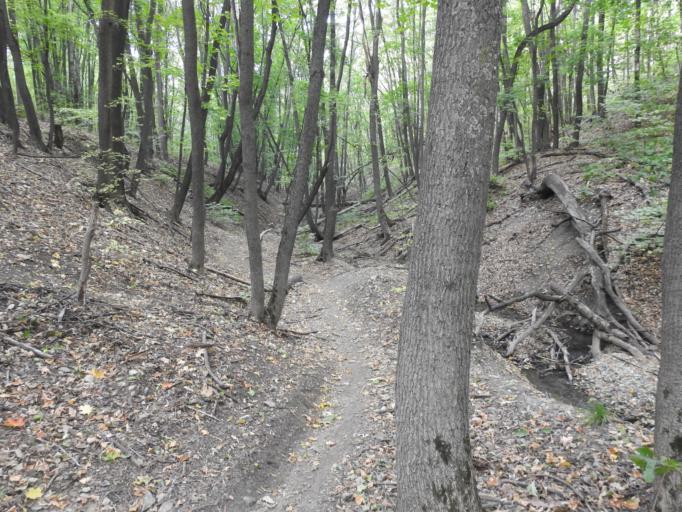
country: RU
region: Saratov
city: Sokolovyy
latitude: 51.5515
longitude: 45.8795
